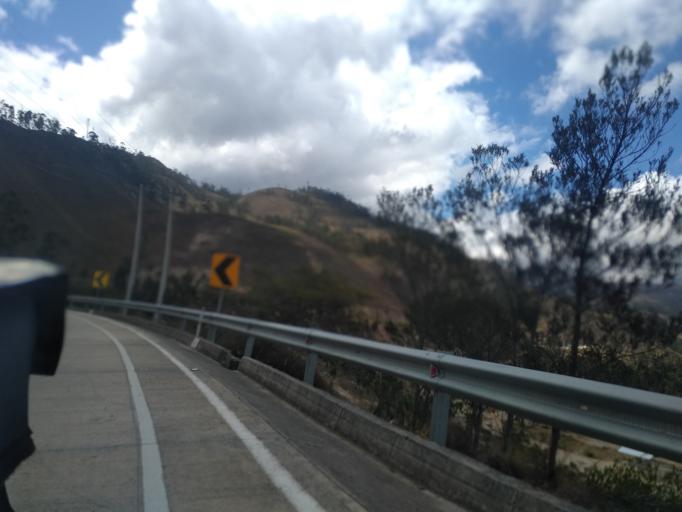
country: EC
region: El Oro
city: Zaruma
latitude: -3.4496
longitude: -79.1663
